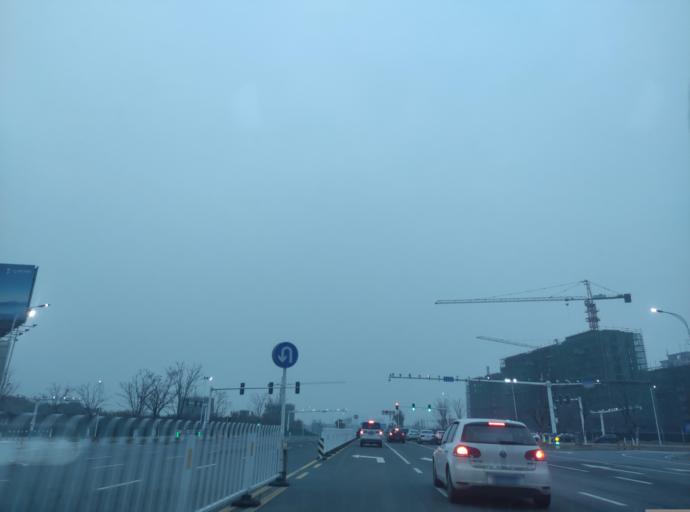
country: CN
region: Jiangxi Sheng
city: Pingxiang
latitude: 27.6713
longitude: 113.8535
